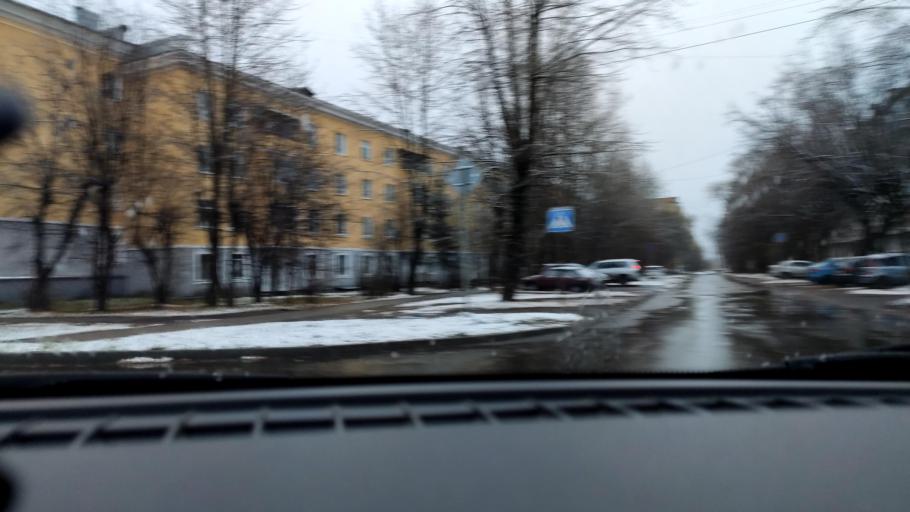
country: RU
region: Perm
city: Kultayevo
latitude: 57.9954
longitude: 55.9414
